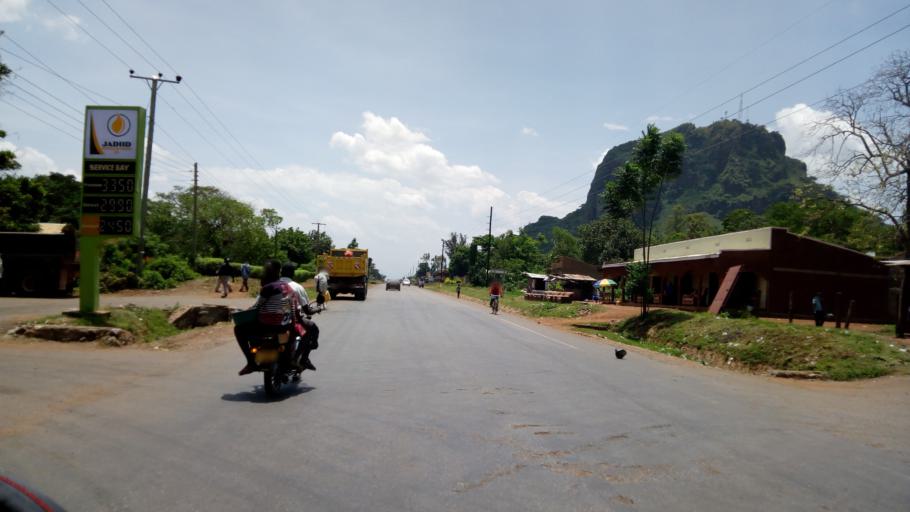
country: UG
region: Eastern Region
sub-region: Tororo District
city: Tororo
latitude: 0.6770
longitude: 34.1770
